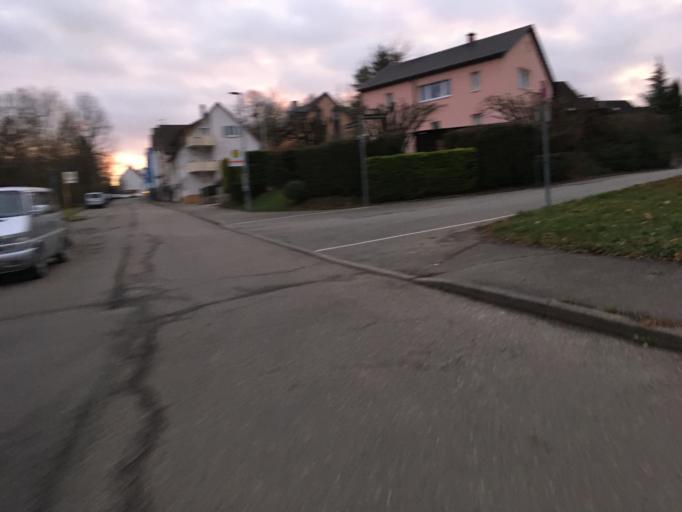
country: DE
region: Baden-Wuerttemberg
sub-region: Regierungsbezirk Stuttgart
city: Kornwestheim
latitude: 48.8432
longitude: 9.2001
